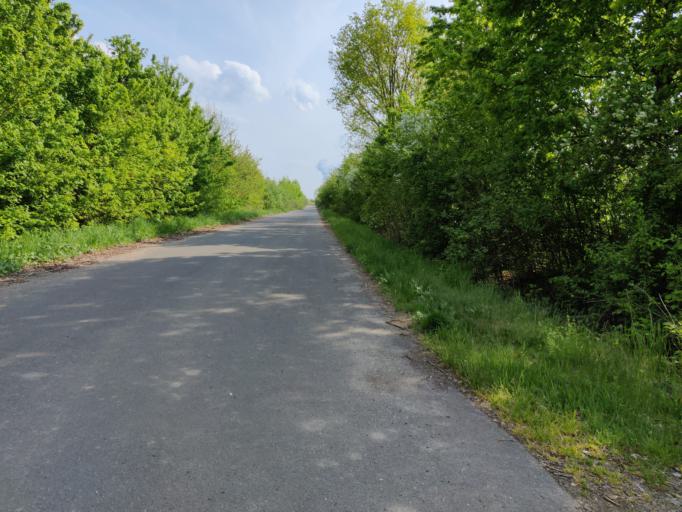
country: DE
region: Saxony
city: Bohlen
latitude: 51.2341
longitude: 12.3679
